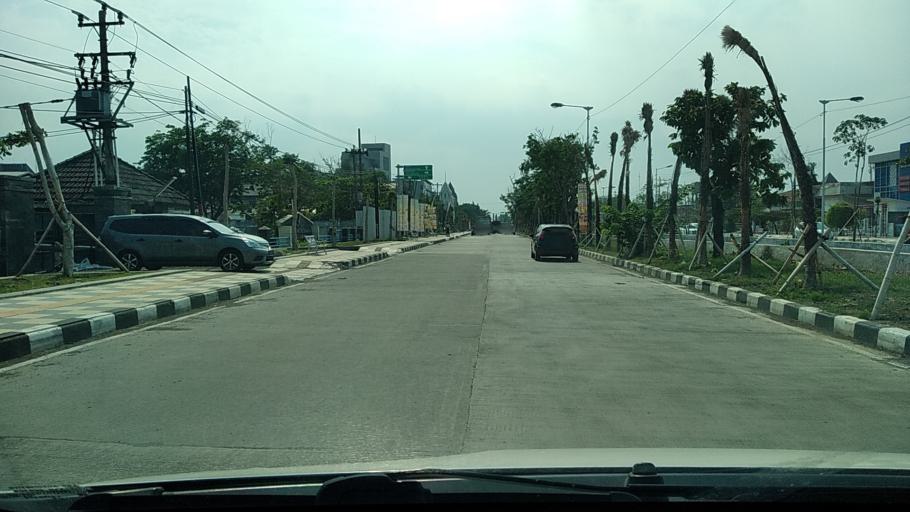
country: ID
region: Central Java
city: Semarang
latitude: -6.9618
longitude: 110.3965
